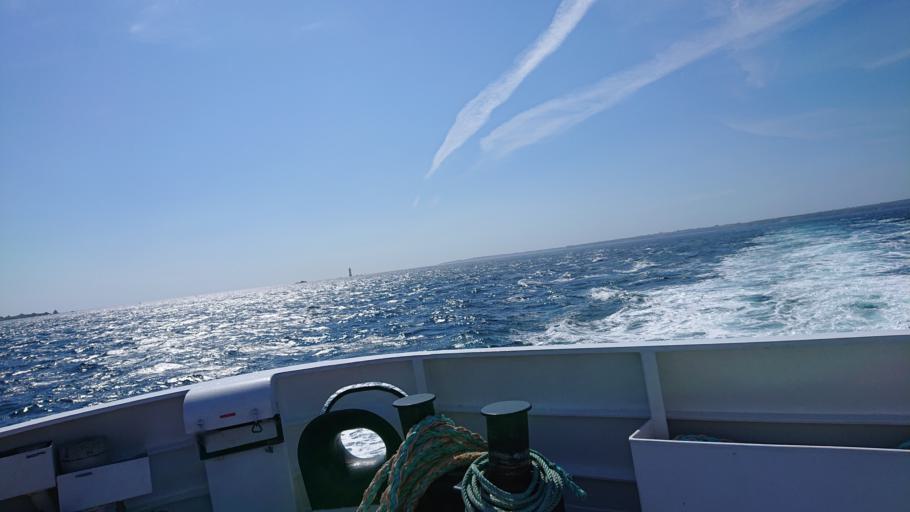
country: FR
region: Brittany
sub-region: Departement du Finistere
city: Lampaul-Plouarzel
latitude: 48.4435
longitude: -4.9880
